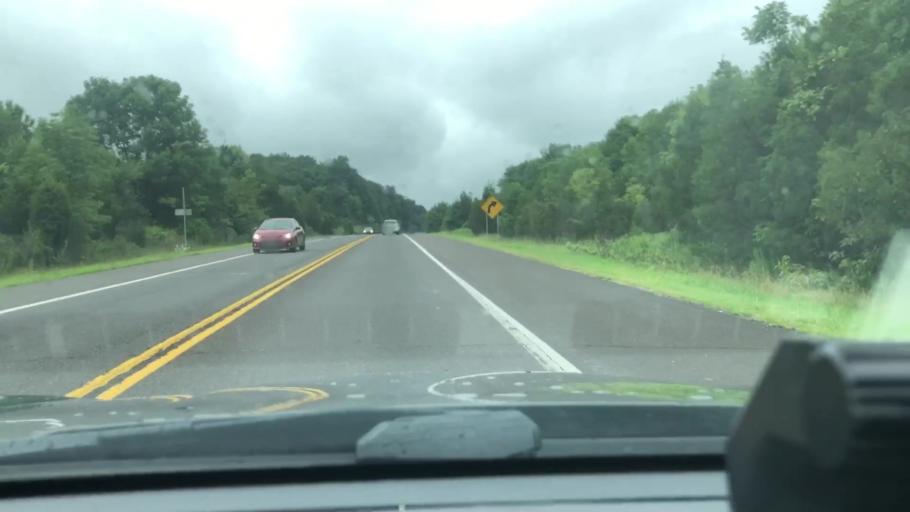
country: US
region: Pennsylvania
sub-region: Bucks County
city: Spinnerstown
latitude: 40.4177
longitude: -75.4547
